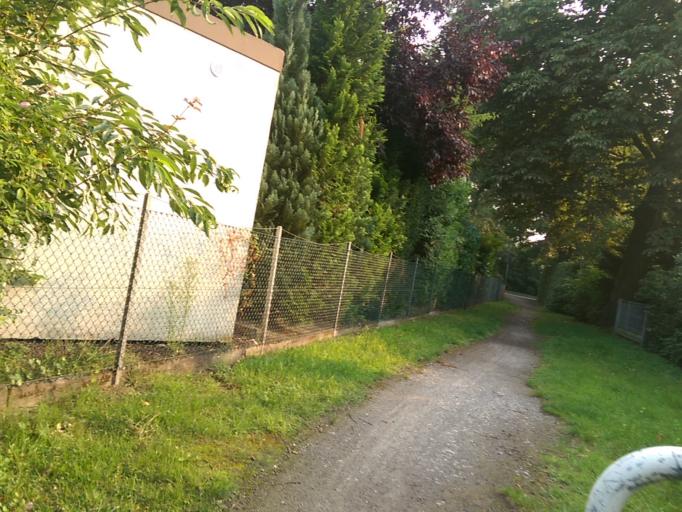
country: DE
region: North Rhine-Westphalia
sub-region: Regierungsbezirk Detmold
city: Guetersloh
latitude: 51.8992
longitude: 8.3586
